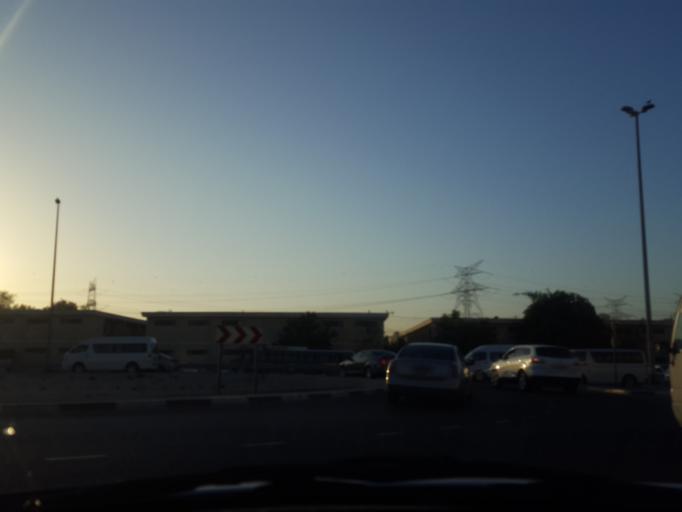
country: AE
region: Dubai
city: Dubai
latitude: 25.1379
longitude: 55.2562
